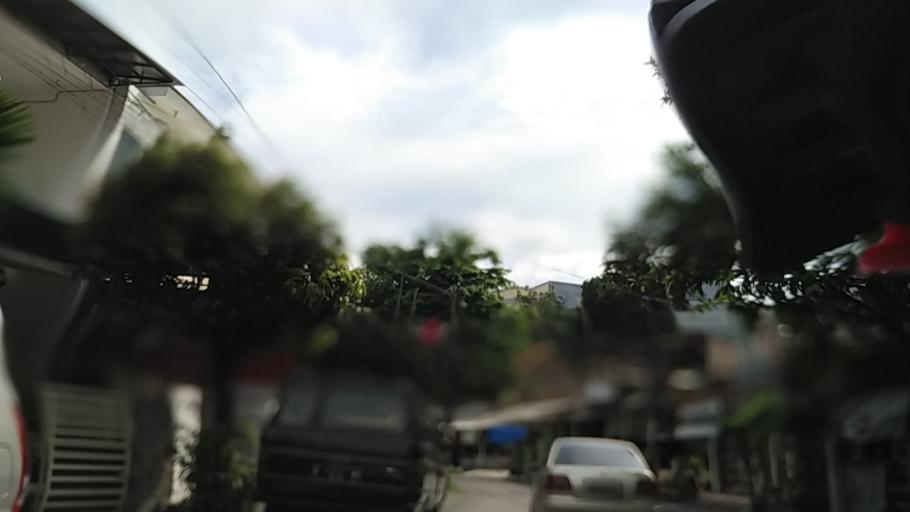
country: ID
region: Central Java
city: Semarang
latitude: -6.9983
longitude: 110.4242
